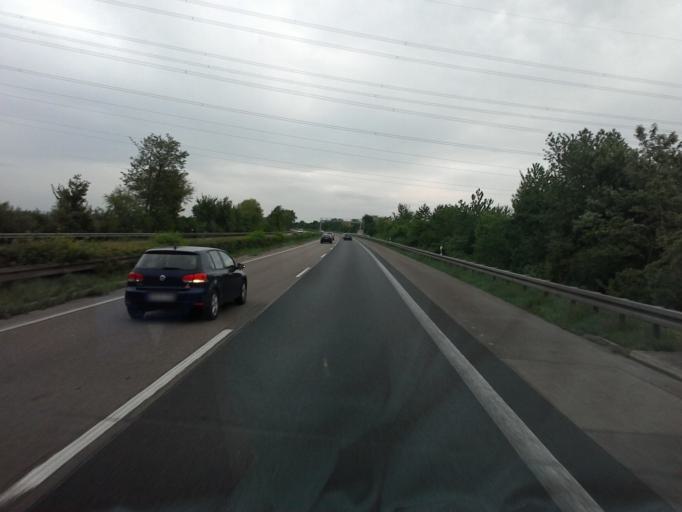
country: DE
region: North Rhine-Westphalia
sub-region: Regierungsbezirk Koln
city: Erftstadt
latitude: 50.8329
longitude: 6.7910
